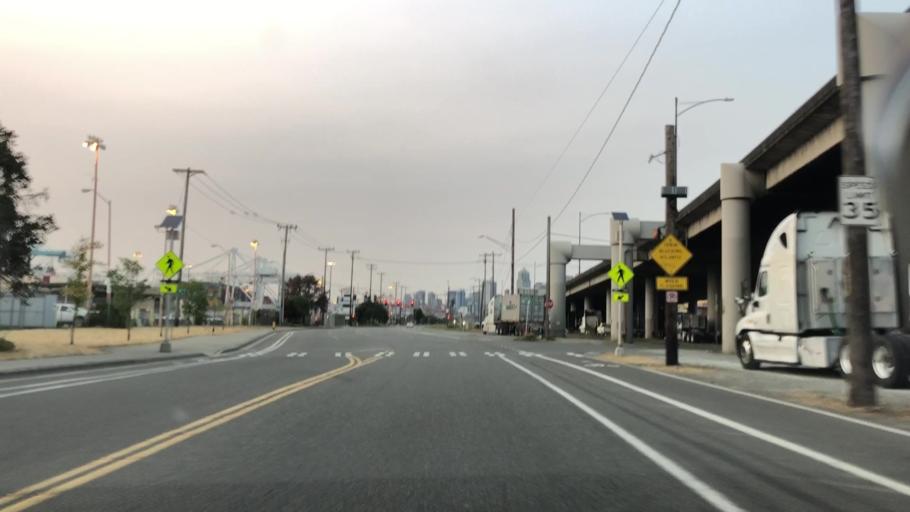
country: US
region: Washington
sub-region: King County
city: Seattle
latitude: 47.5740
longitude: -122.3398
